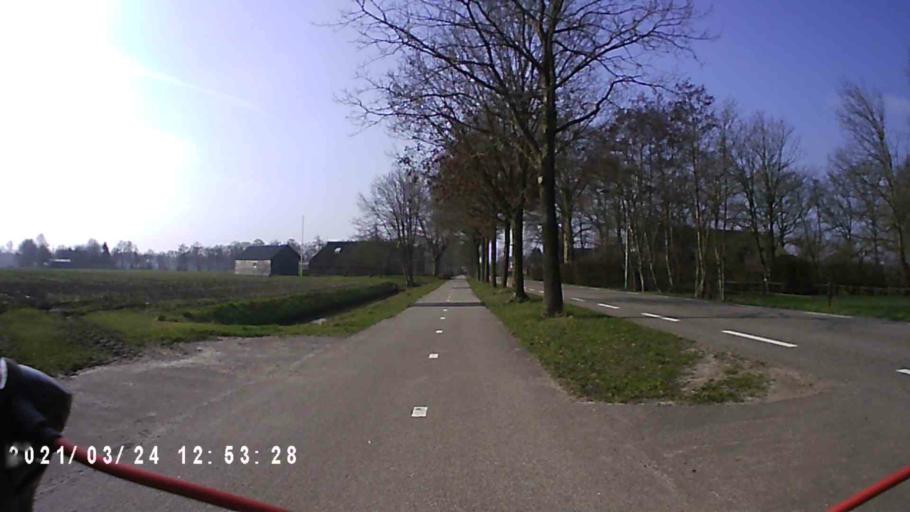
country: NL
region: Groningen
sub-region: Gemeente Leek
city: Leek
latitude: 53.1565
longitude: 6.3189
